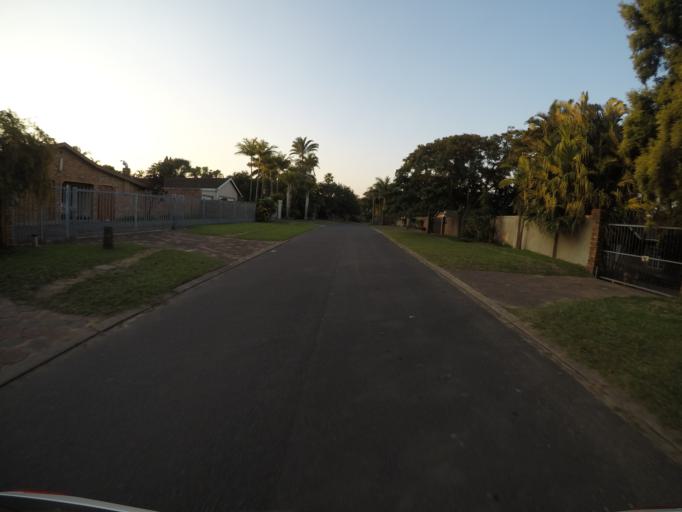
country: ZA
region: KwaZulu-Natal
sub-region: uThungulu District Municipality
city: Richards Bay
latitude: -28.7685
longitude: 32.1156
